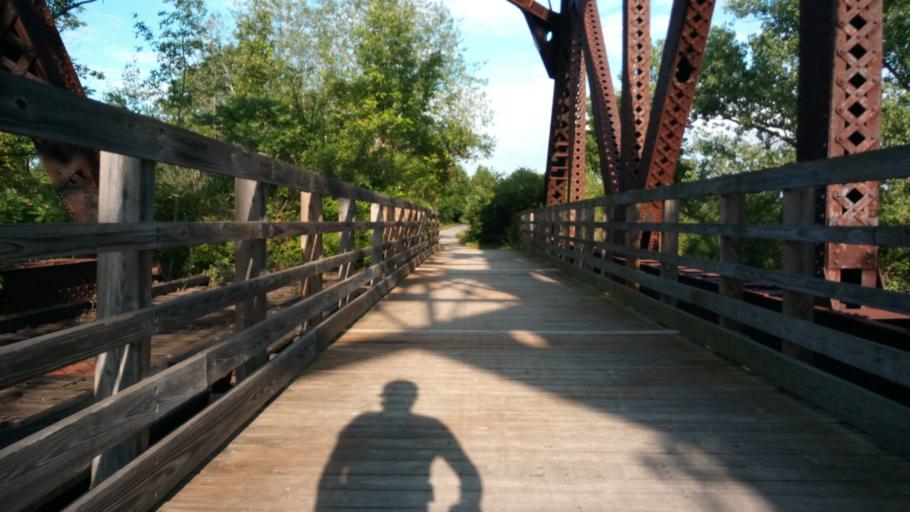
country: US
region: New York
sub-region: Ontario County
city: Victor
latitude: 43.0004
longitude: -77.4502
